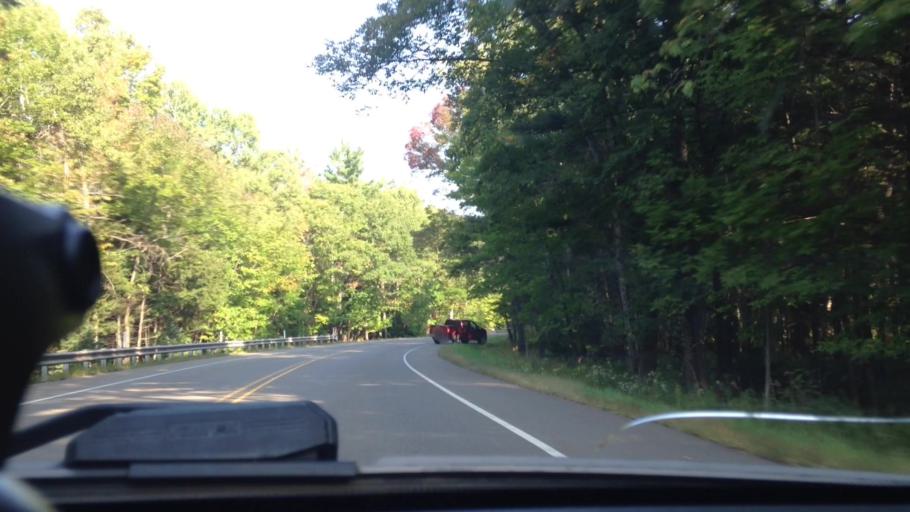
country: US
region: Michigan
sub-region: Dickinson County
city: Quinnesec
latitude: 45.8190
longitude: -87.9880
